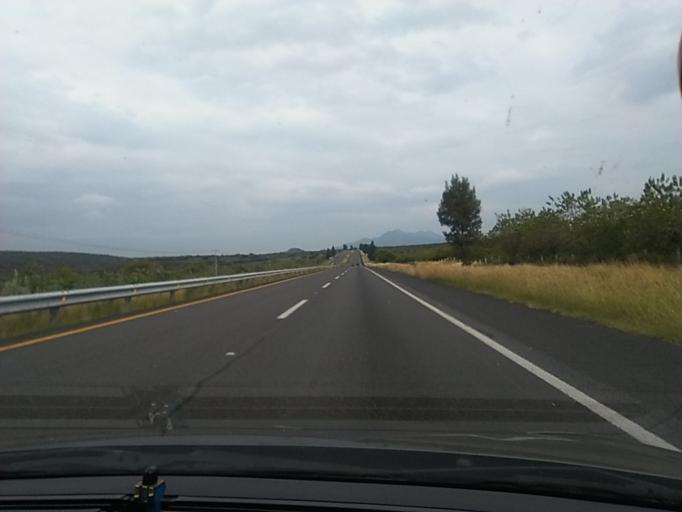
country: MX
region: Michoacan
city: Ecuandureo
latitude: 20.1704
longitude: -102.1481
